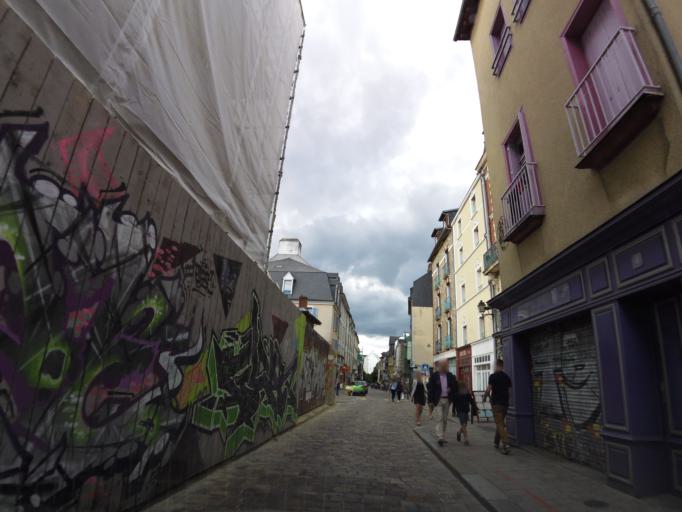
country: FR
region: Brittany
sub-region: Departement d'Ille-et-Vilaine
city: Rennes
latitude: 48.1154
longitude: -1.6809
